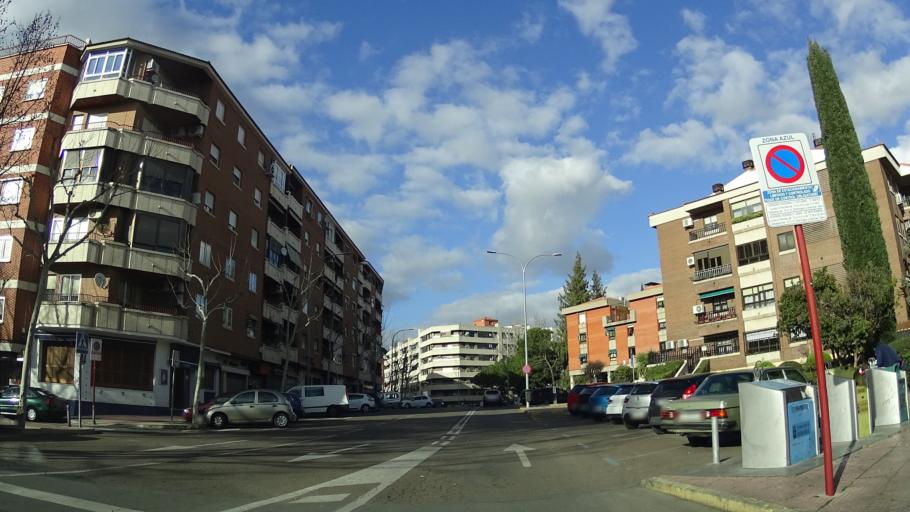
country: ES
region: Castille-La Mancha
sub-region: Provincia de Ciudad Real
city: Ciudad Real
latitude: 38.9829
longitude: -3.9257
